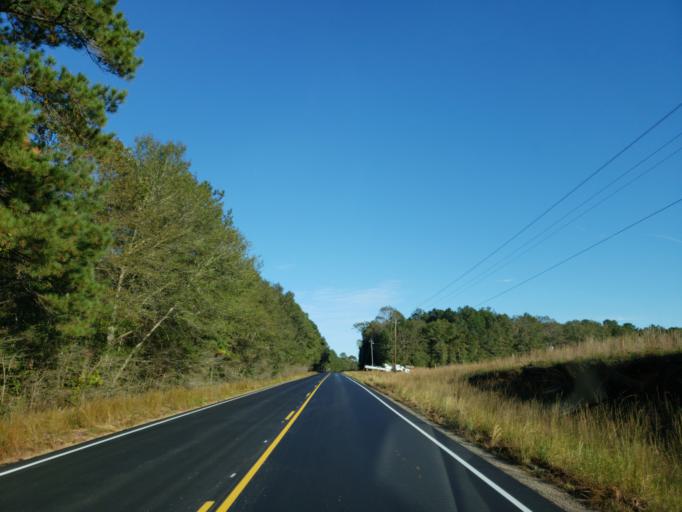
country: US
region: Mississippi
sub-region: Perry County
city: Richton
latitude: 31.3748
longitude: -88.8307
